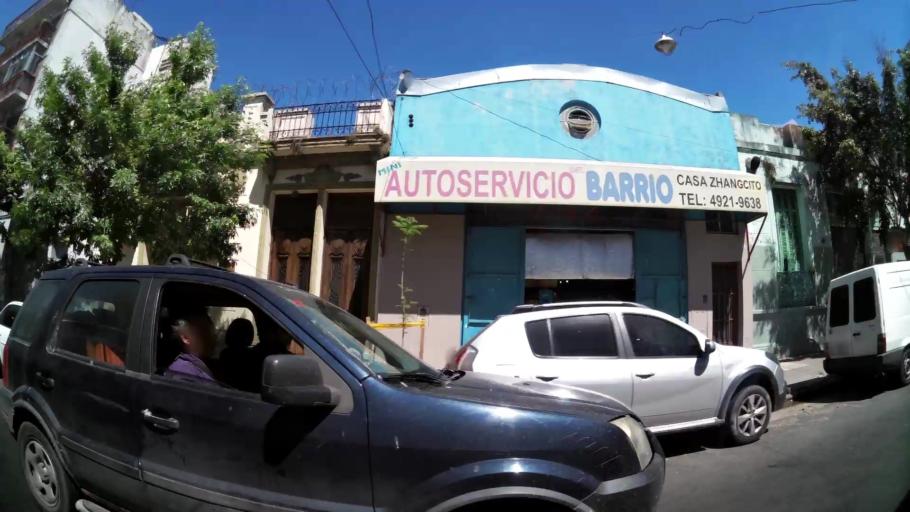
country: AR
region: Buenos Aires F.D.
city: Buenos Aires
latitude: -34.6336
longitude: -58.4193
